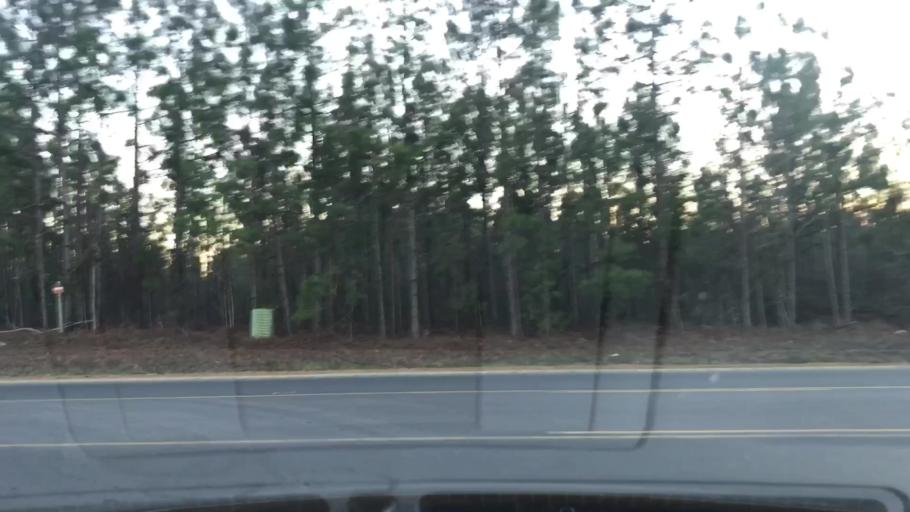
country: US
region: North Carolina
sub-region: Brunswick County
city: Shallotte
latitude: 33.9805
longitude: -78.4135
